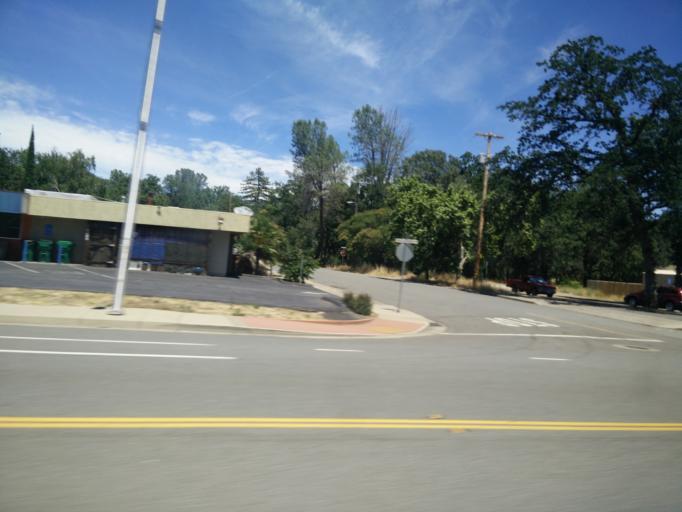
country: US
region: California
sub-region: Shasta County
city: Shasta Lake
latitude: 40.6804
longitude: -122.3603
